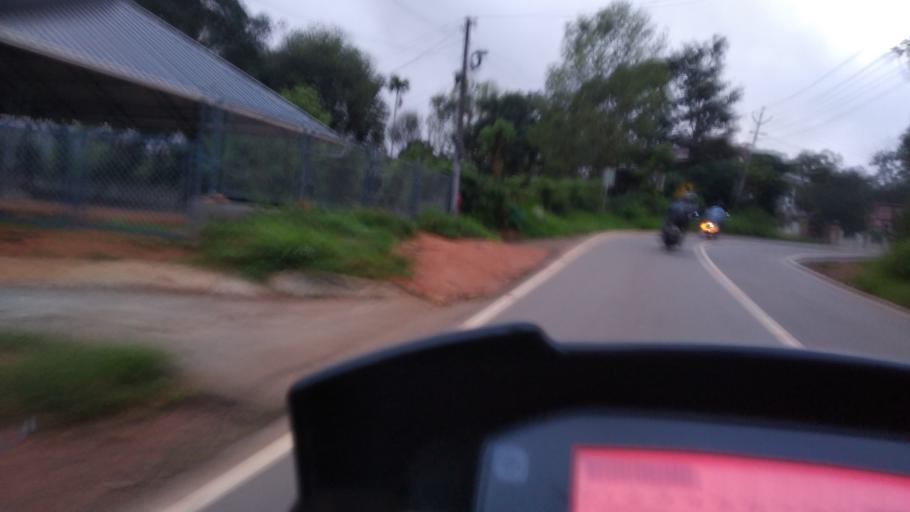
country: IN
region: Kerala
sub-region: Idukki
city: Munnar
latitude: 9.9690
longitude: 77.1131
